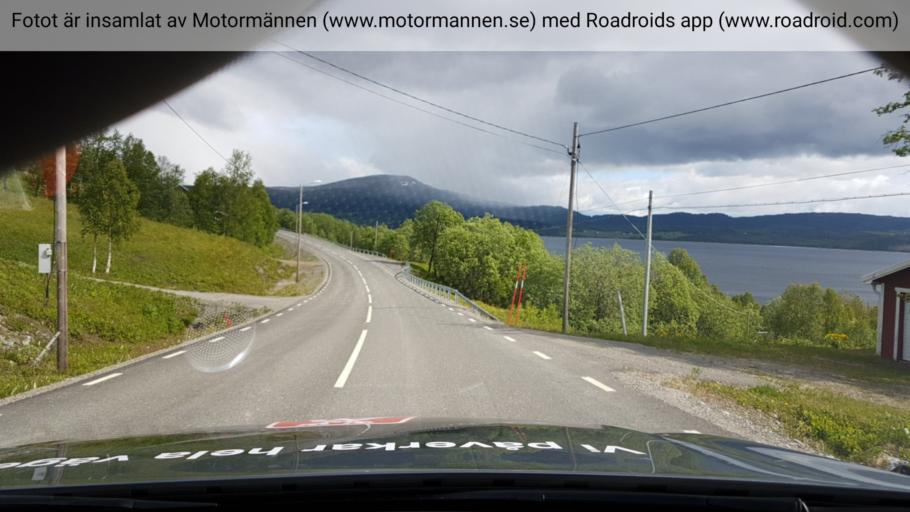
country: NO
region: Nord-Trondelag
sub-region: Royrvik
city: Royrvik
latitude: 64.7978
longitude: 14.0639
